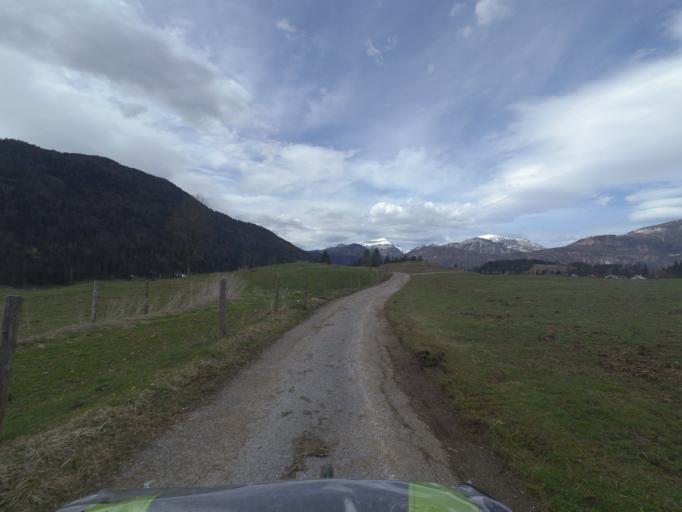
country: AT
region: Salzburg
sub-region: Politischer Bezirk Hallein
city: Abtenau
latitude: 47.5675
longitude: 13.3337
